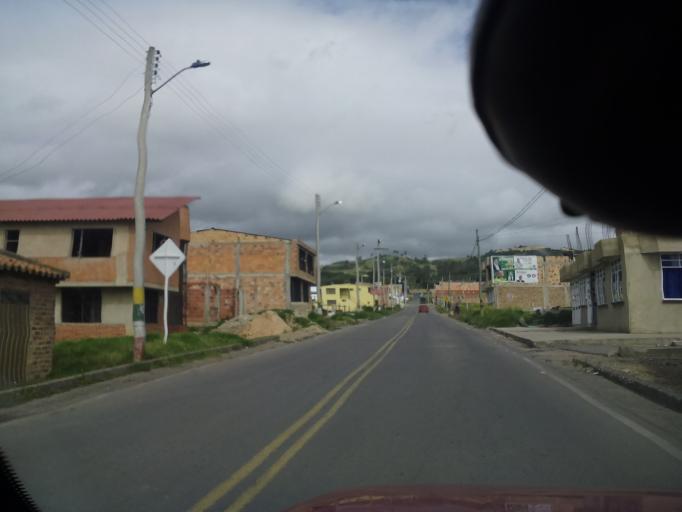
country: CO
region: Boyaca
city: Combita
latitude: 5.6328
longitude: -73.3220
